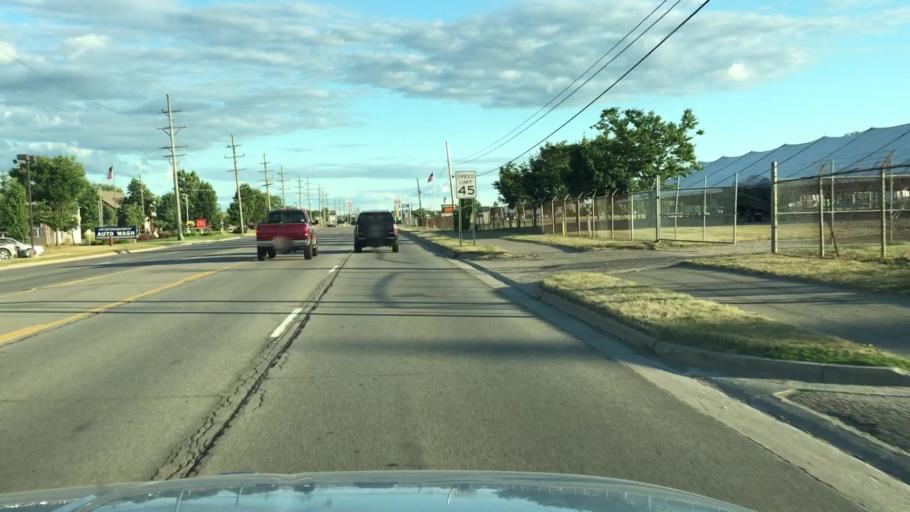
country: US
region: Michigan
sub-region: Lapeer County
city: Imlay City
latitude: 43.0173
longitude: -83.0721
